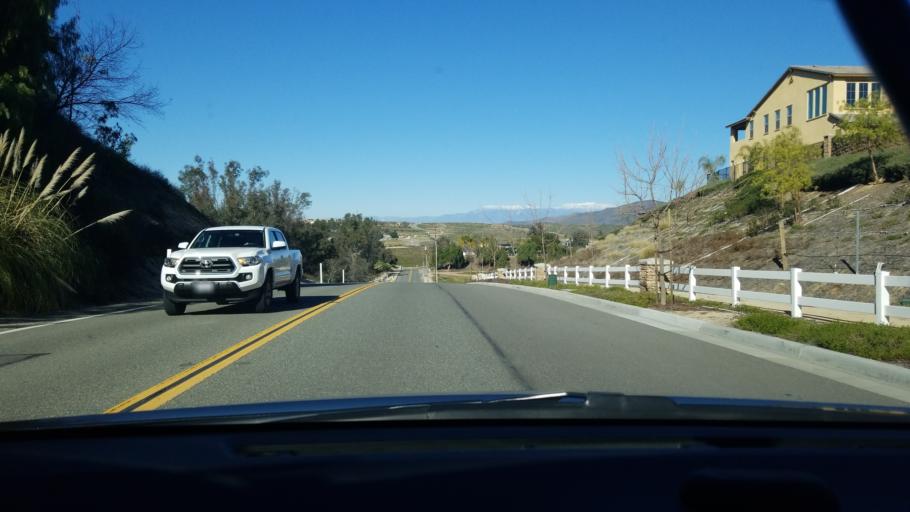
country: US
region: California
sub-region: Riverside County
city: Murrieta Hot Springs
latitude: 33.5369
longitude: -117.1037
